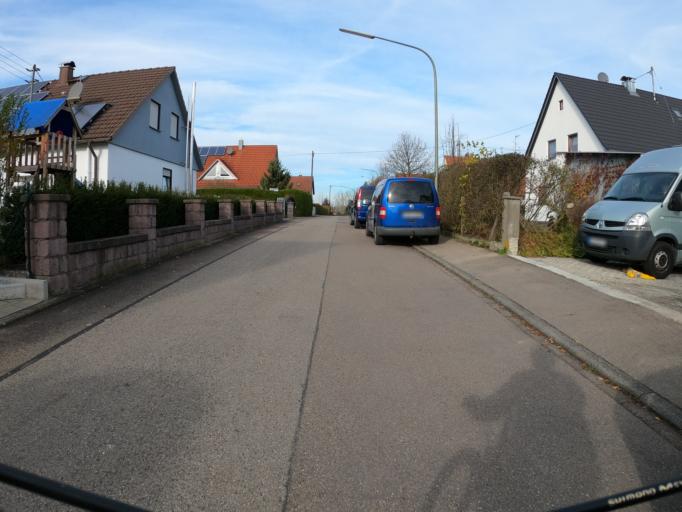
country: DE
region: Bavaria
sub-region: Swabia
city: Nersingen
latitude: 48.4298
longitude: 10.1626
